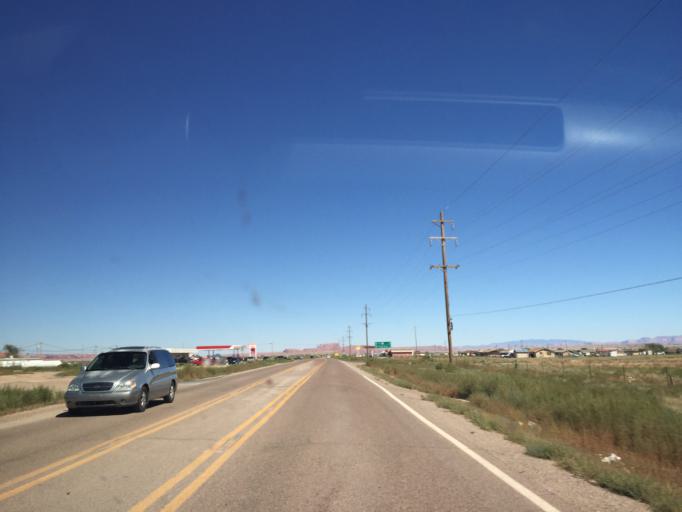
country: US
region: Arizona
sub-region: Apache County
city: Many Farms
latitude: 36.3513
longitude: -109.6186
